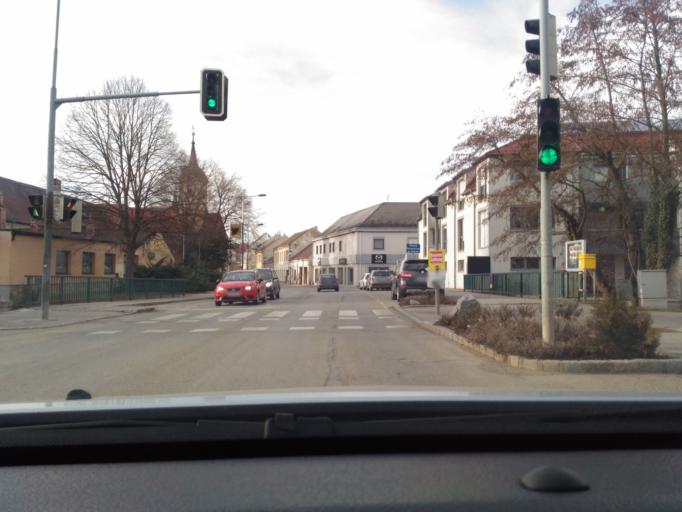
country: AT
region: Lower Austria
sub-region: Politischer Bezirk Mistelbach
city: Laa an der Thaya
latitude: 48.7193
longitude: 16.3879
